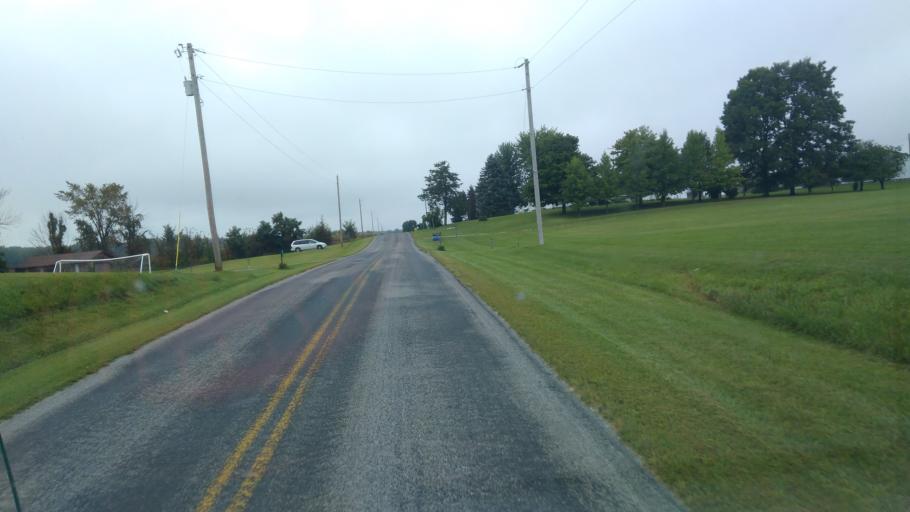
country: US
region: Ohio
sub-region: Hardin County
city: Kenton
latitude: 40.5589
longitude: -83.6362
